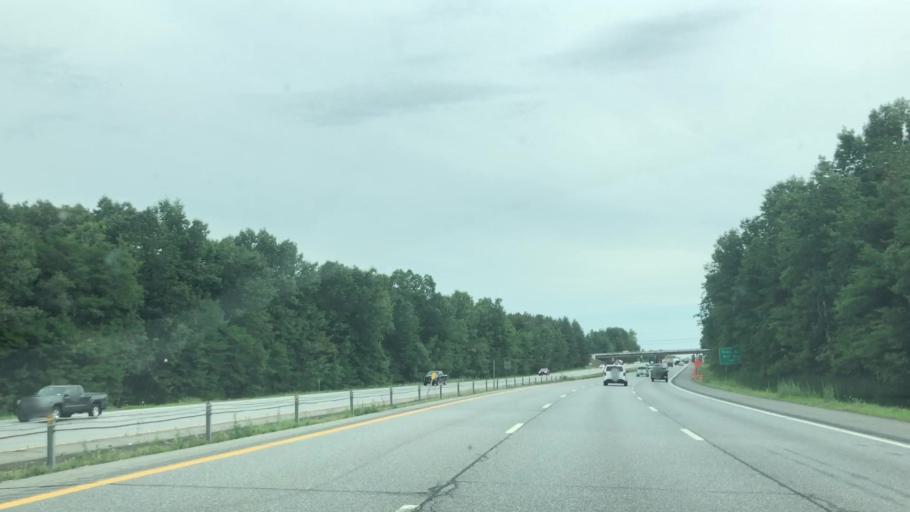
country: US
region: New York
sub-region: Warren County
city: West Glens Falls
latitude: 43.3131
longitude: -73.6750
